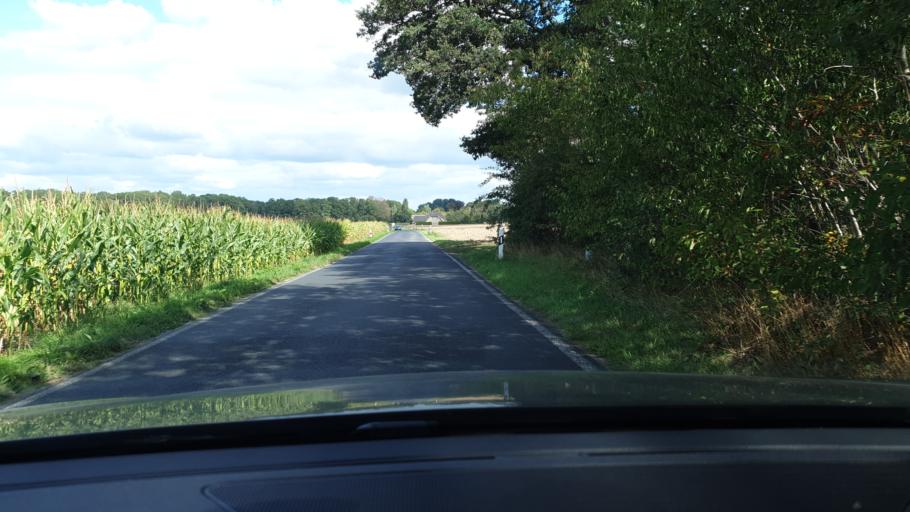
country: NL
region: Gelderland
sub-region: Gemeente Groesbeek
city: De Horst
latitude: 51.7710
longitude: 5.9925
